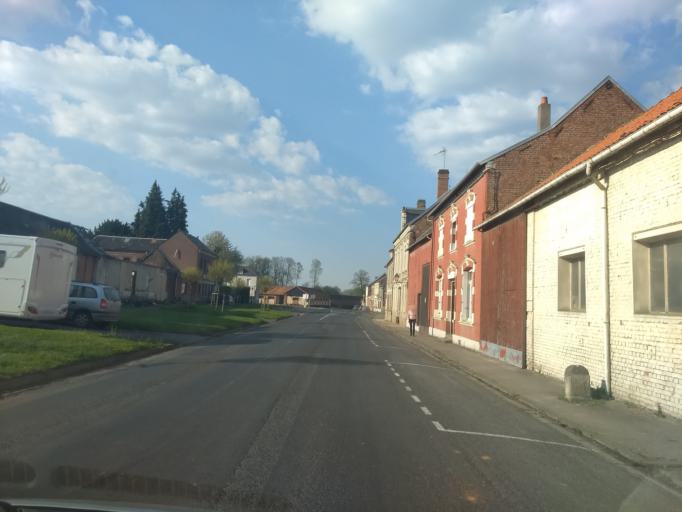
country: FR
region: Picardie
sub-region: Departement de la Somme
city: Albert
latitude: 50.0795
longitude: 2.6028
